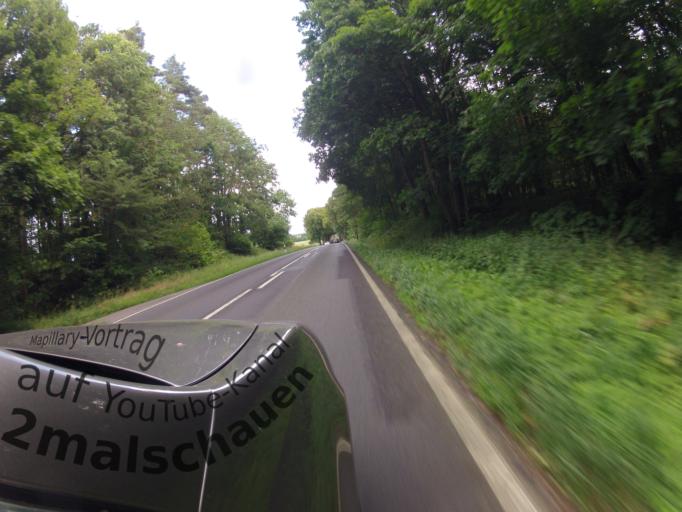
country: DE
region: Mecklenburg-Vorpommern
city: Usedom
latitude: 53.9056
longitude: 14.0350
